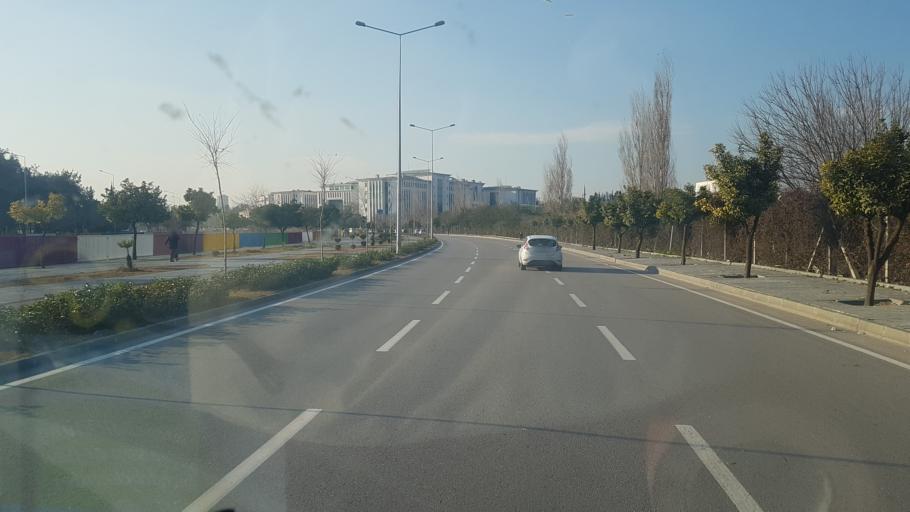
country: TR
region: Adana
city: Adana
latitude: 37.0119
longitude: 35.3516
